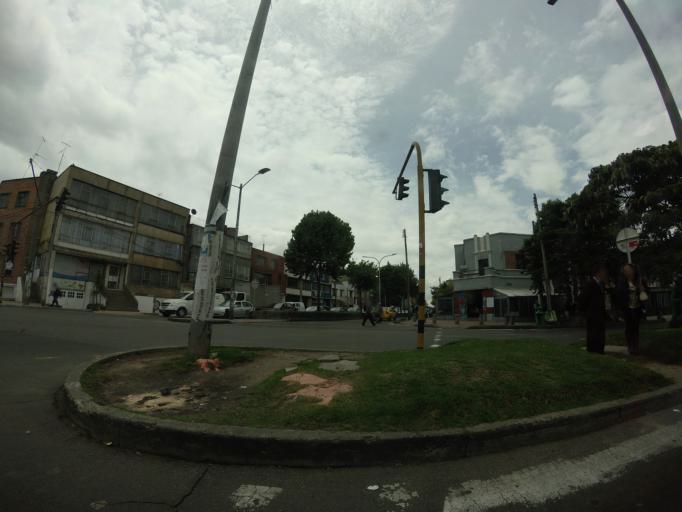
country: CO
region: Bogota D.C.
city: Bogota
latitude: 4.6243
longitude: -74.0764
